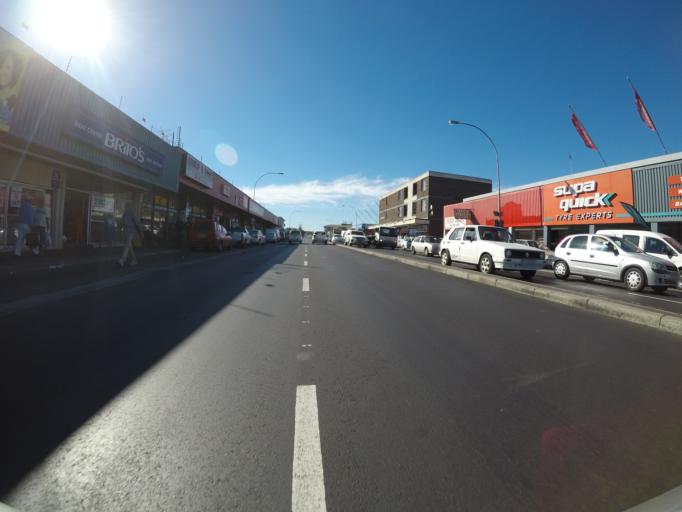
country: ZA
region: Western Cape
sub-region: City of Cape Town
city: Kraaifontein
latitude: -33.9237
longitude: 18.6775
